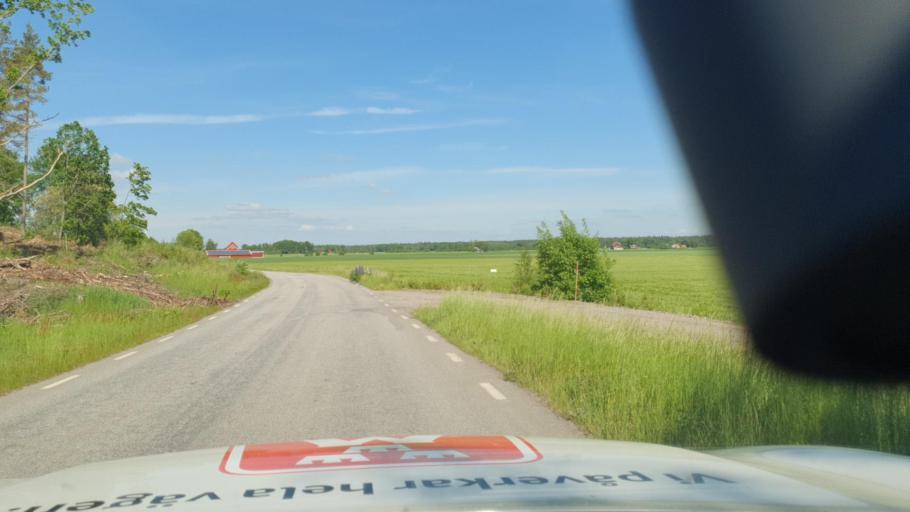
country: SE
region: Vaestra Goetaland
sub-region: Grastorps Kommun
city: Graestorp
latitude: 58.2958
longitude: 12.7708
